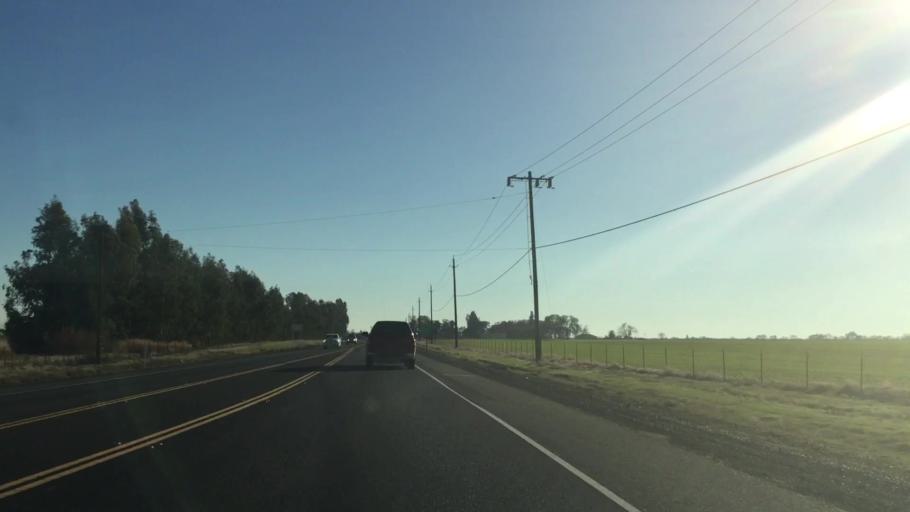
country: US
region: California
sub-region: Butte County
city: Palermo
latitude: 39.4150
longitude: -121.6050
